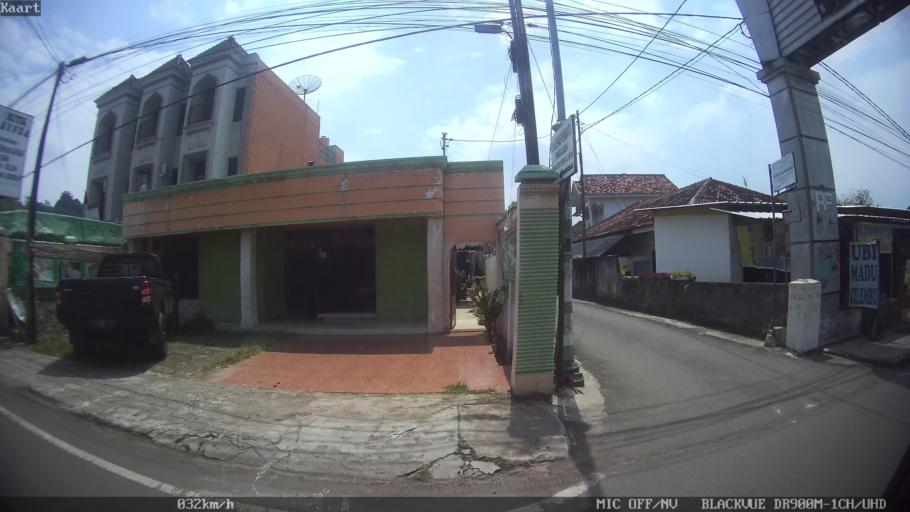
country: ID
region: Lampung
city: Bandarlampung
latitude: -5.4311
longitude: 105.2535
